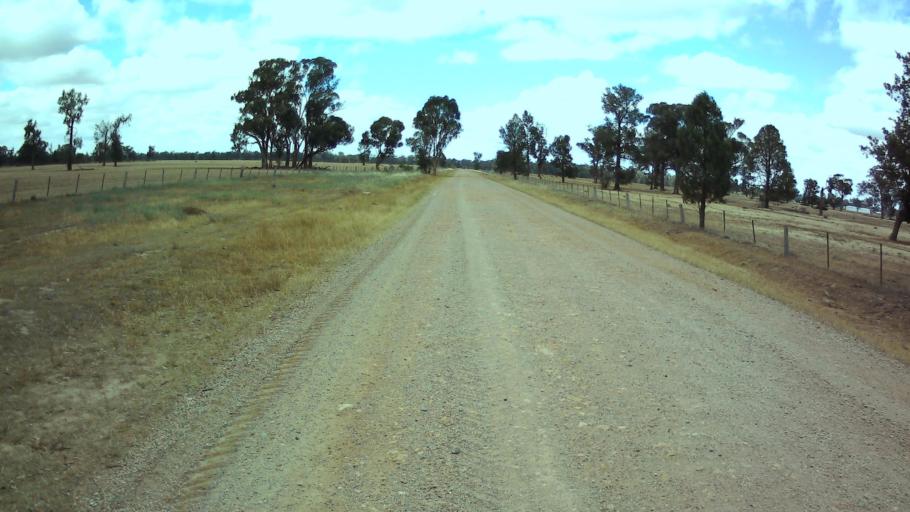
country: AU
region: New South Wales
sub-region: Weddin
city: Grenfell
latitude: -34.0192
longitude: 147.9148
